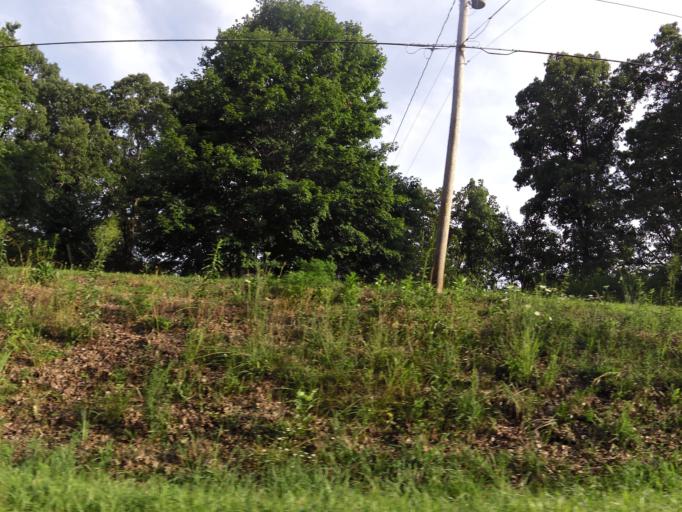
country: US
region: Tennessee
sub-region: Dickson County
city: Dickson
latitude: 36.0888
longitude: -87.4630
